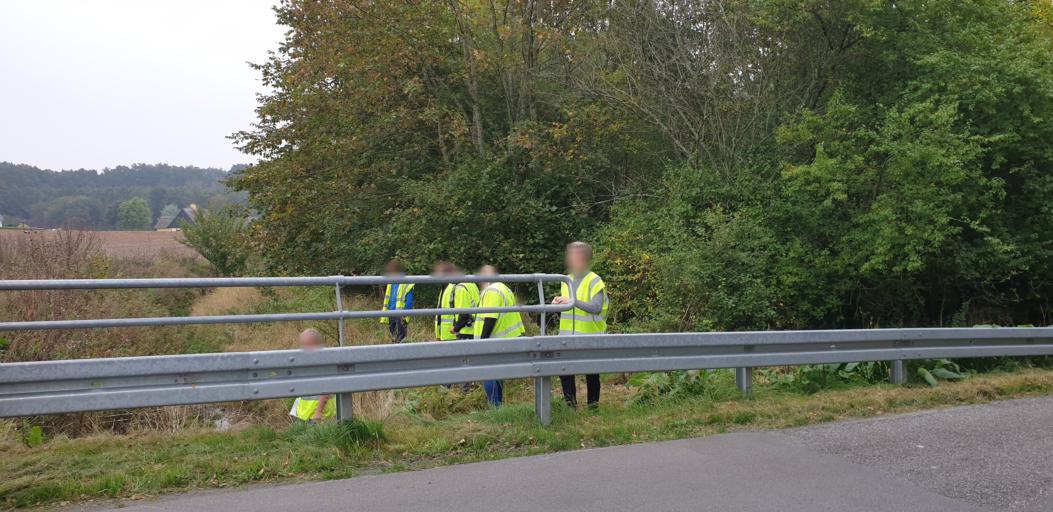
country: DK
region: Zealand
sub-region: Koge Kommune
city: Koge
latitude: 55.3739
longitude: 12.1136
